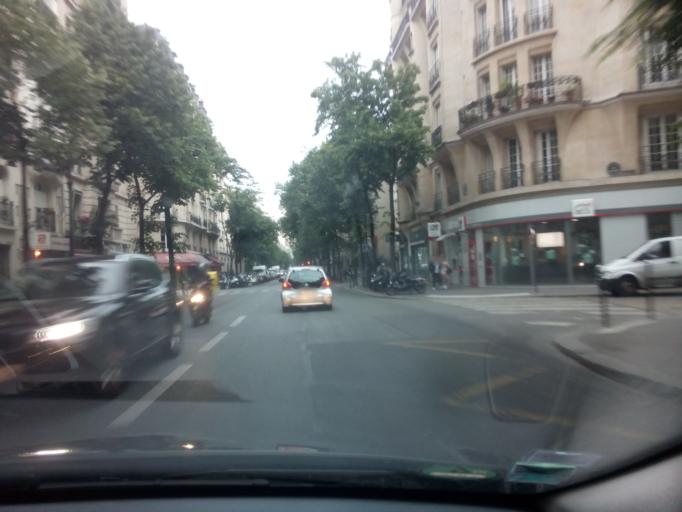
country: FR
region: Ile-de-France
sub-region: Departement des Hauts-de-Seine
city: Vanves
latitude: 48.8410
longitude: 2.2882
